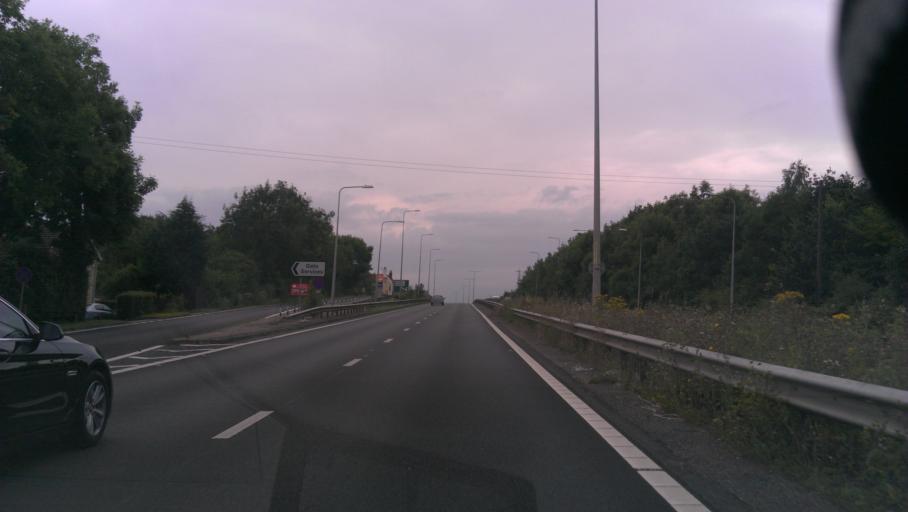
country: GB
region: England
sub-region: Kent
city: Dunkirk
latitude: 51.2892
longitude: 0.9999
